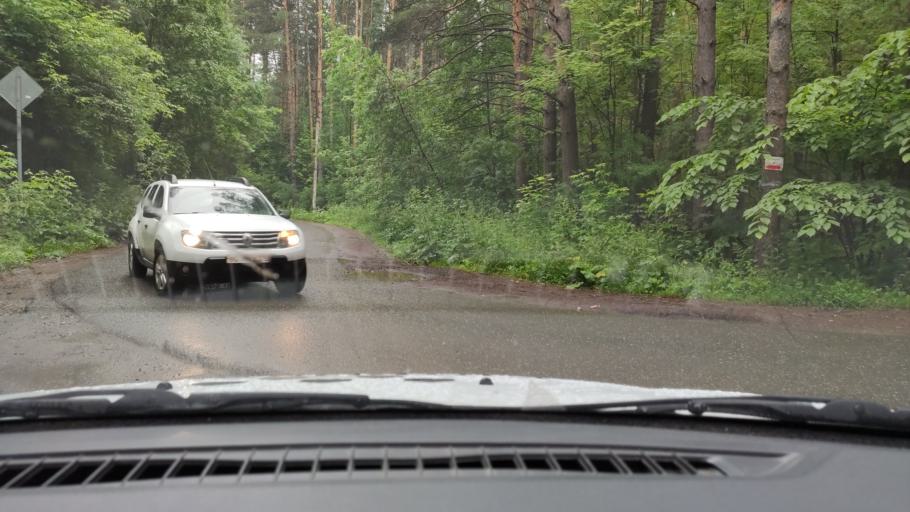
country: RU
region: Udmurtiya
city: Izhevsk
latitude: 56.8849
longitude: 53.1866
